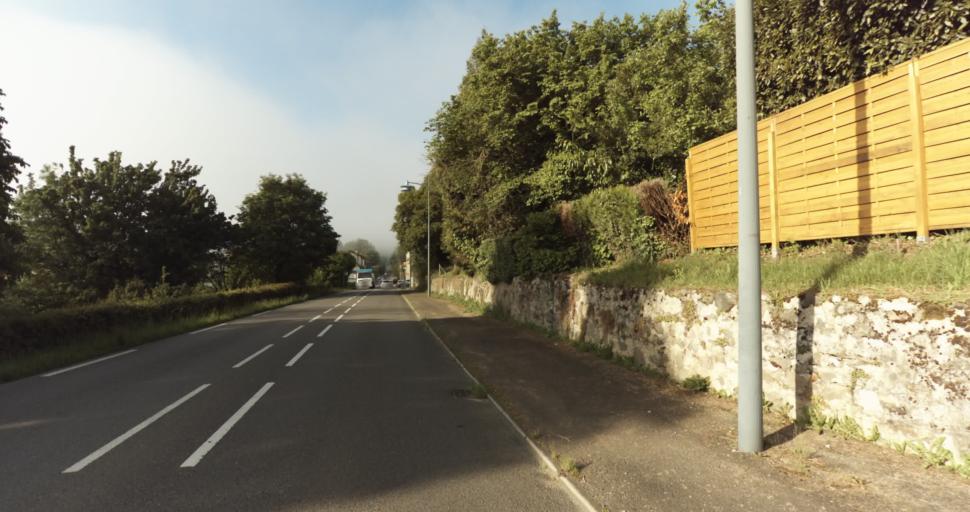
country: FR
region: Limousin
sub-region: Departement de la Haute-Vienne
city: Le Vigen
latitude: 45.7528
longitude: 1.2899
